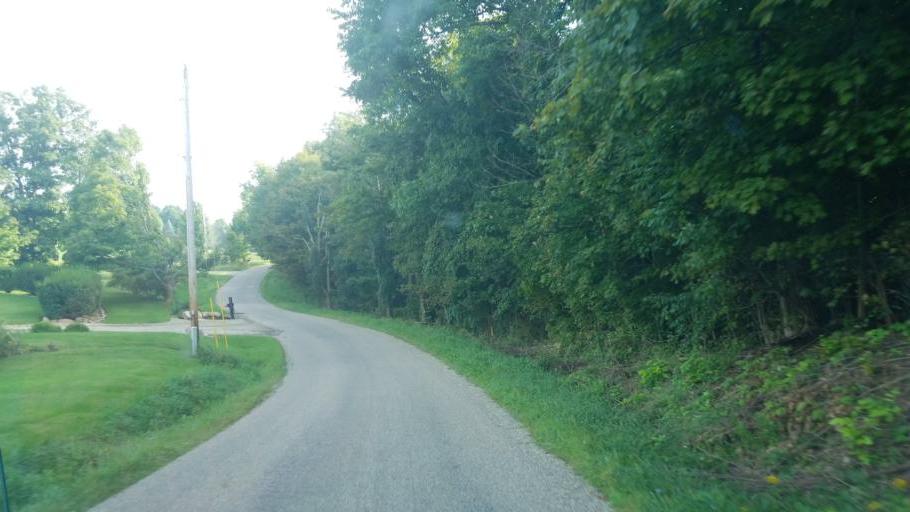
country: US
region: Ohio
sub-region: Medina County
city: Lodi
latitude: 40.9494
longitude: -82.0045
